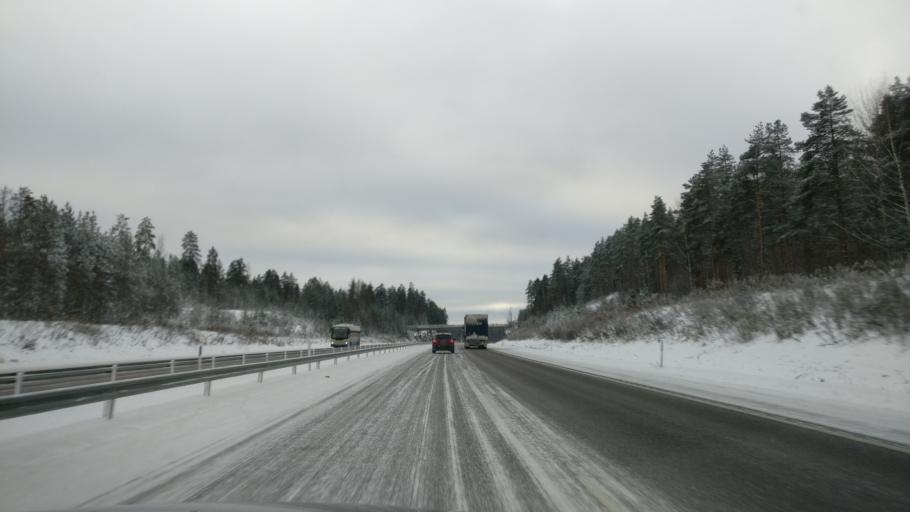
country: FI
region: Paijanne Tavastia
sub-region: Lahti
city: Nastola
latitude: 61.0128
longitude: 25.8215
